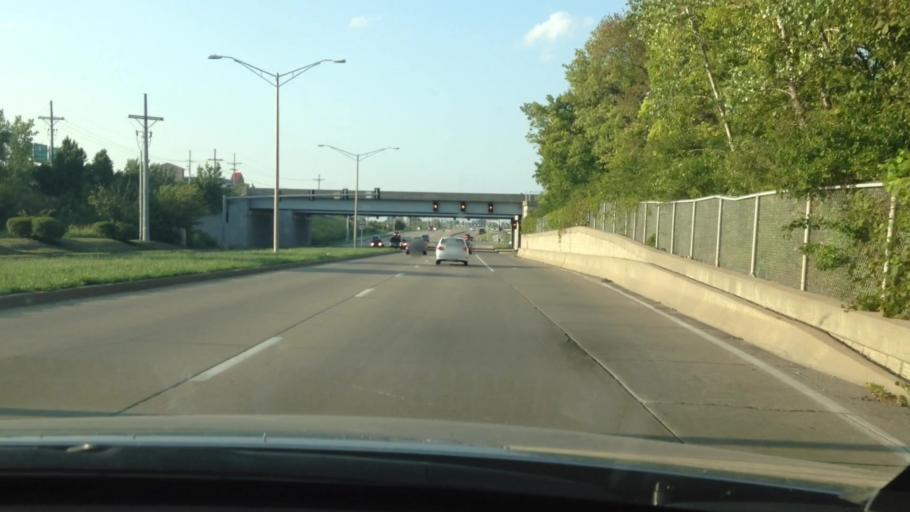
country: US
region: Missouri
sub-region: Platte County
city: Weatherby Lake
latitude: 39.2530
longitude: -94.6495
